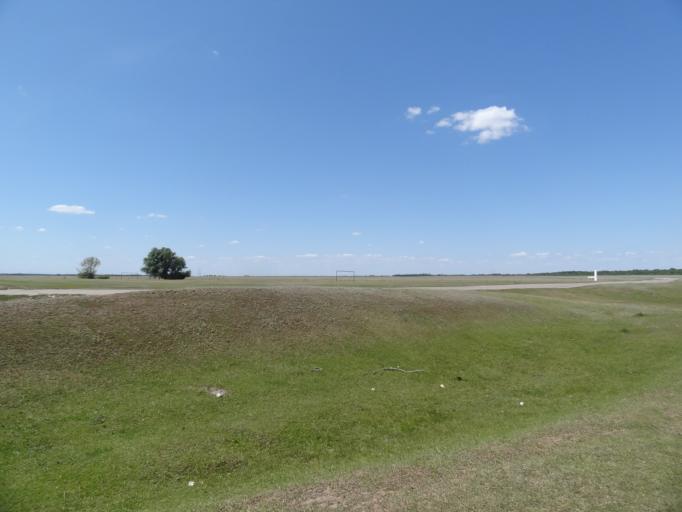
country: RU
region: Saratov
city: Sovetskoye
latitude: 51.2876
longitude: 46.6518
